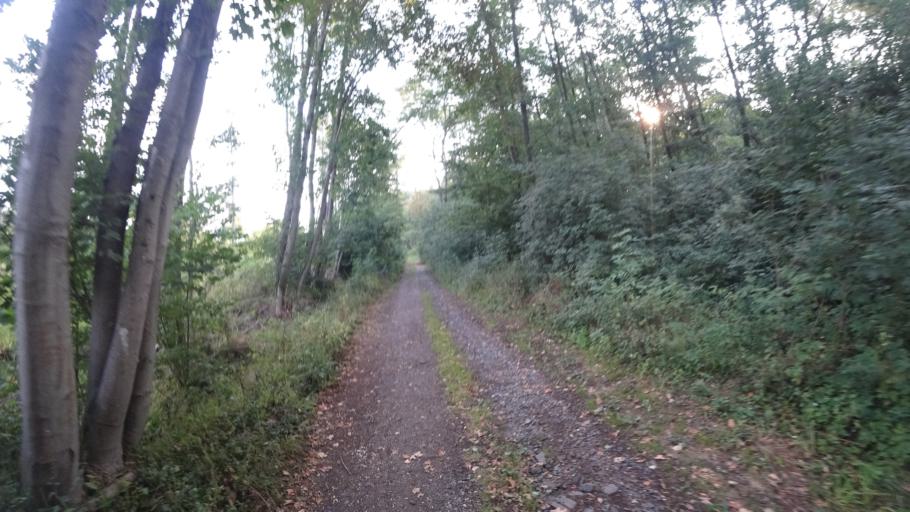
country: DE
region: Rheinland-Pfalz
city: Hohr-Grenzhausen
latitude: 50.4335
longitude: 7.6393
